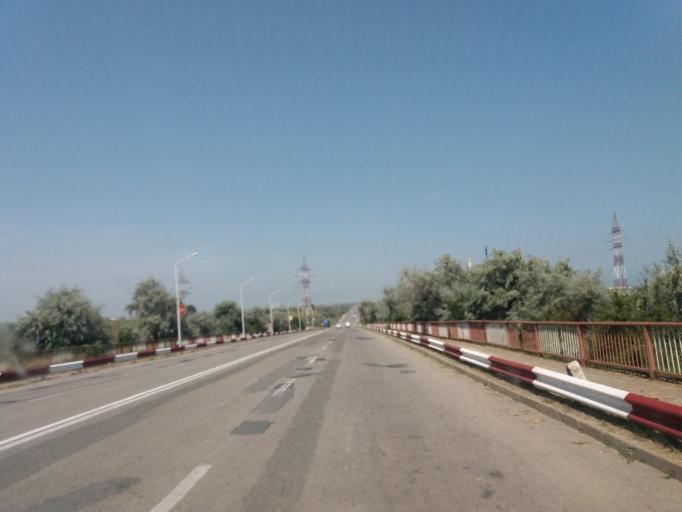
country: RO
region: Constanta
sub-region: Comuna Navodari
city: Navodari
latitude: 44.3232
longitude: 28.6228
